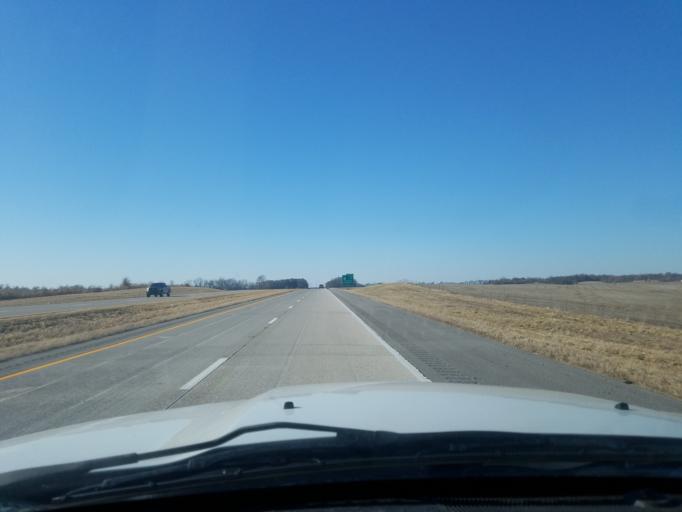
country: US
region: Kentucky
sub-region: Henderson County
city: Henderson
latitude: 37.8031
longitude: -87.5225
